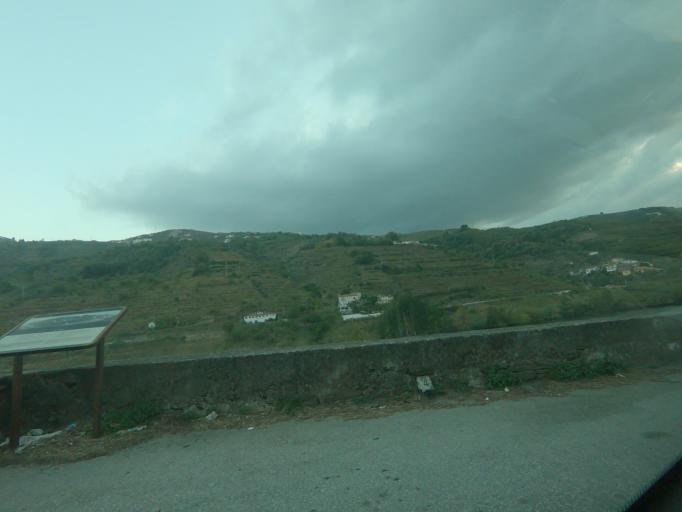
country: PT
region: Vila Real
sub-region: Mesao Frio
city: Mesao Frio
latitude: 41.1932
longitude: -7.9037
